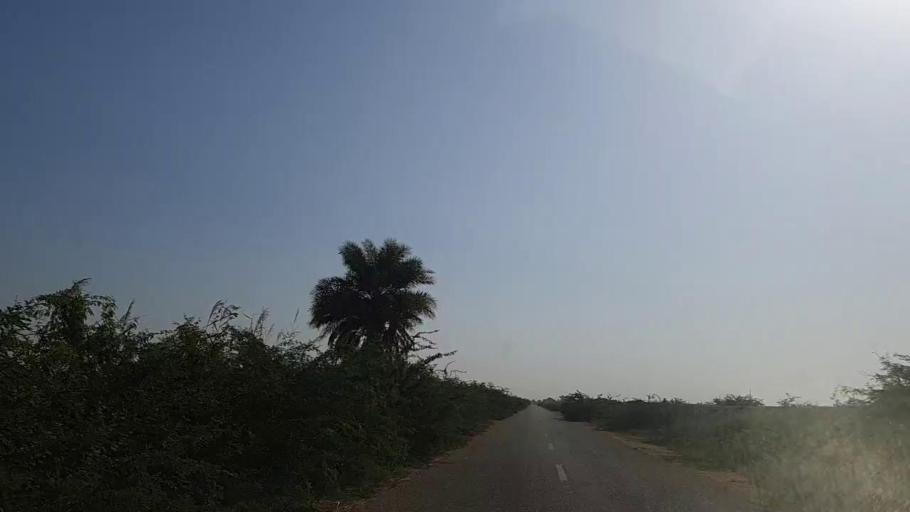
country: PK
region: Sindh
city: Jati
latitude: 24.4361
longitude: 68.2602
